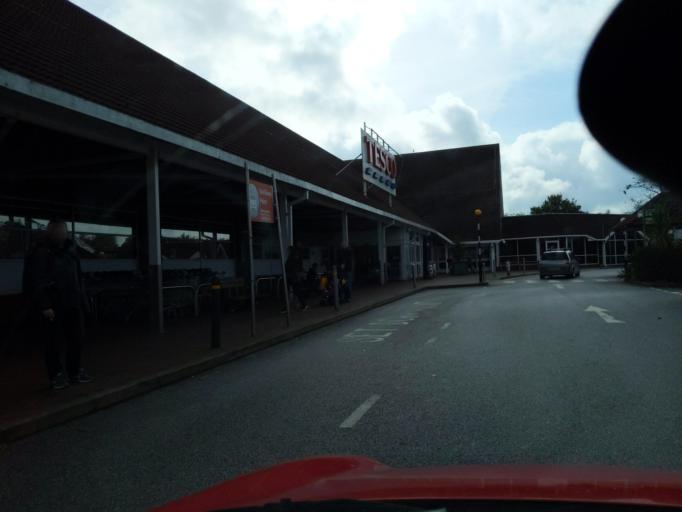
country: GB
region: England
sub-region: Plymouth
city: Plymouth
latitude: 50.4101
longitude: -4.1500
